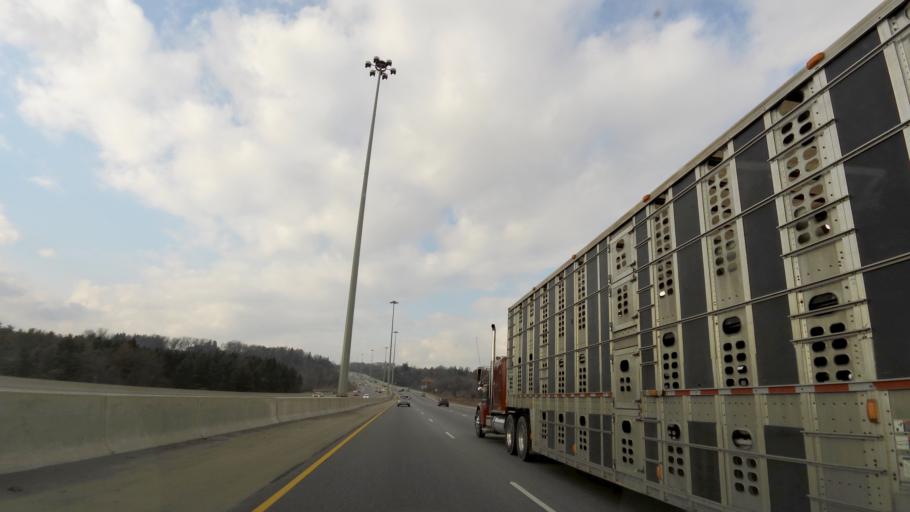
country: CA
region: Ontario
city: Kitchener
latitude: 43.4166
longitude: -80.4095
